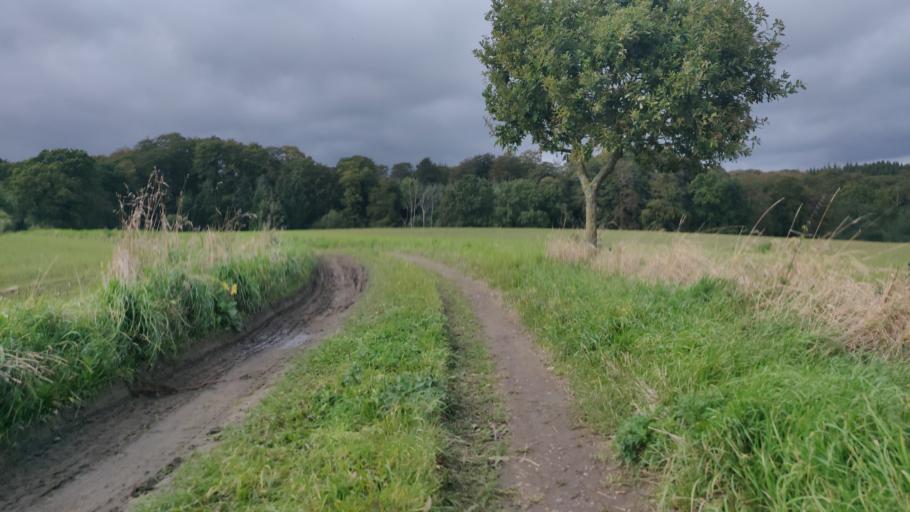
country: DK
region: South Denmark
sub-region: Kolding Kommune
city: Lunderskov
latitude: 55.5390
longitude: 9.3636
